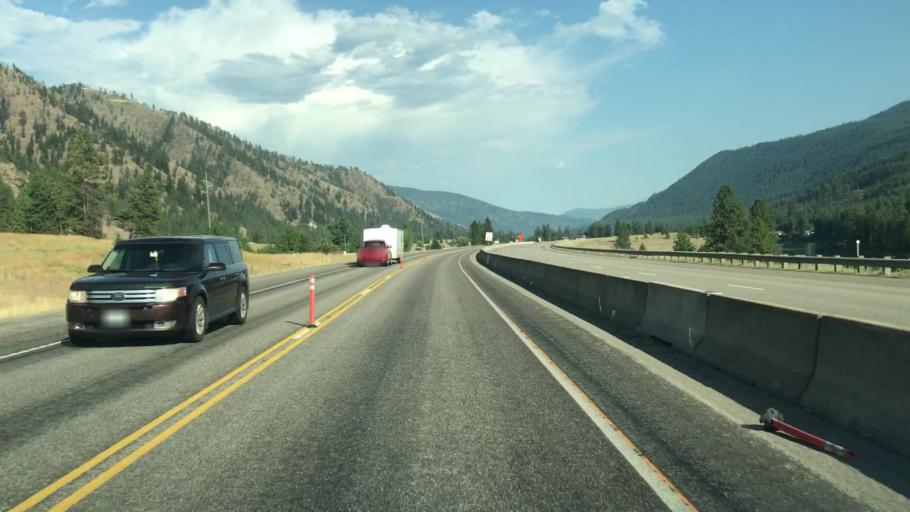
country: US
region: Montana
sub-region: Mineral County
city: Superior
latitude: 47.2154
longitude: -114.9464
